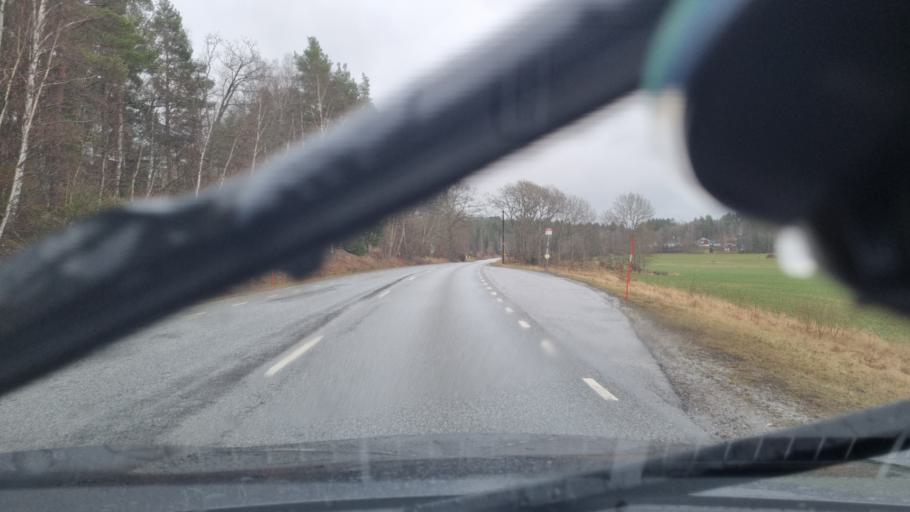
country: SE
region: Stockholm
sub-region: Sigtuna Kommun
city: Sigtuna
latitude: 59.5831
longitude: 17.6702
